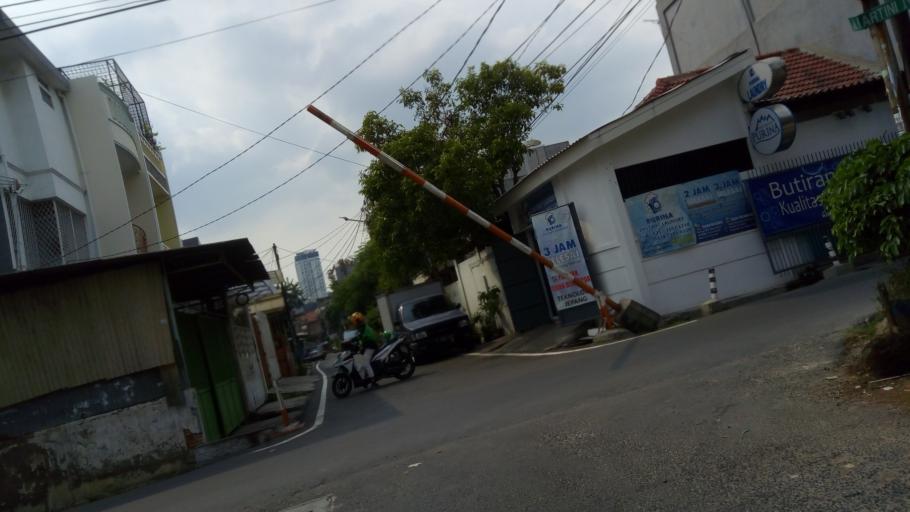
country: ID
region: Jakarta Raya
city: Jakarta
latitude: -6.1557
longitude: 106.8353
